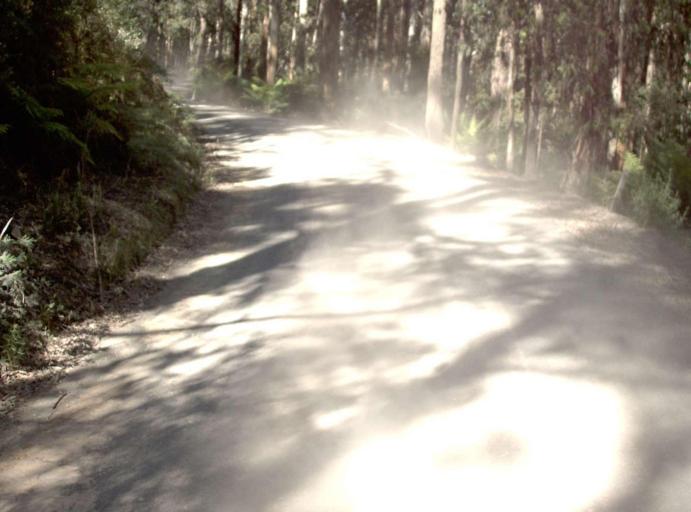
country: AU
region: New South Wales
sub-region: Bombala
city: Bombala
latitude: -37.2450
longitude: 148.7534
